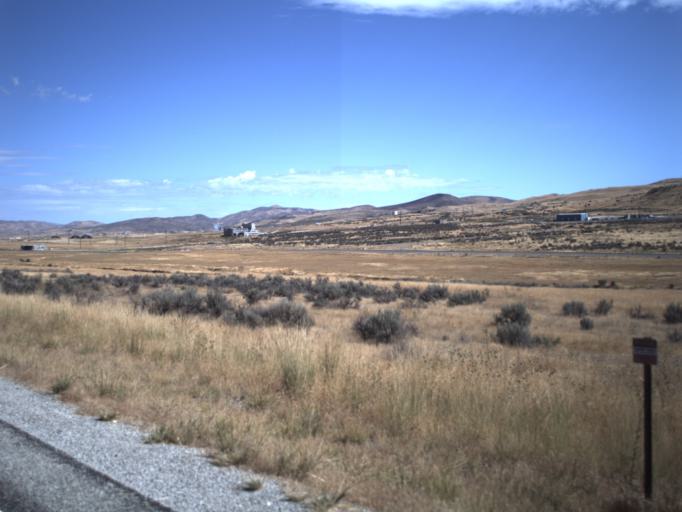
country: US
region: Utah
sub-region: Box Elder County
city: Tremonton
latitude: 41.6844
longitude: -112.4442
